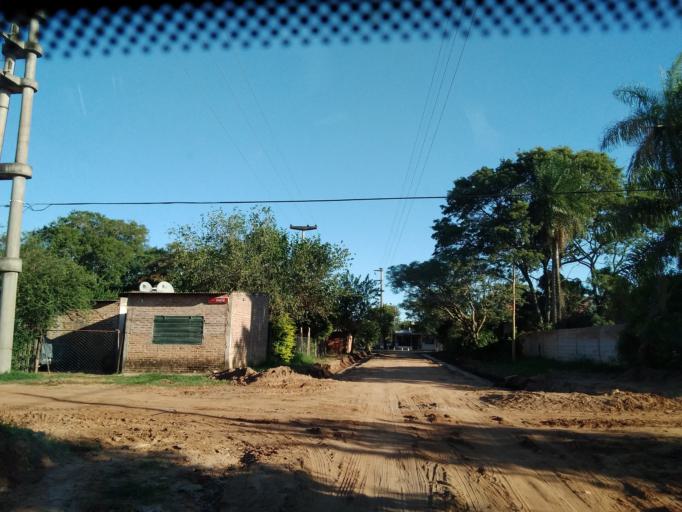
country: AR
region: Corrientes
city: Corrientes
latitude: -27.5059
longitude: -58.7943
